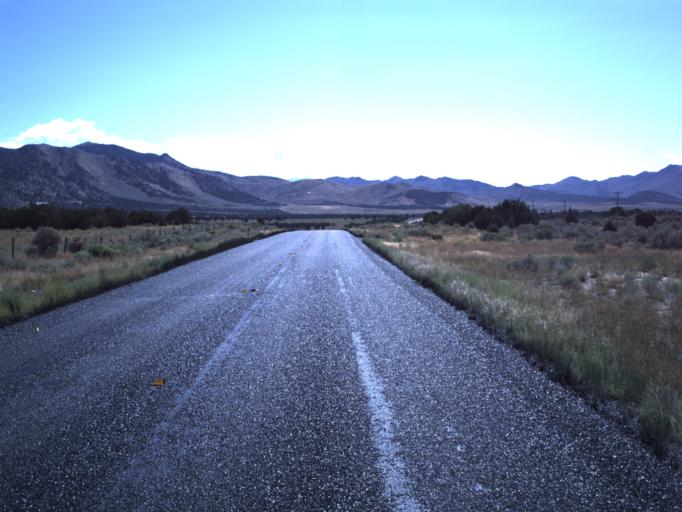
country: US
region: Utah
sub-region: Utah County
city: Genola
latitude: 39.9417
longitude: -112.1914
